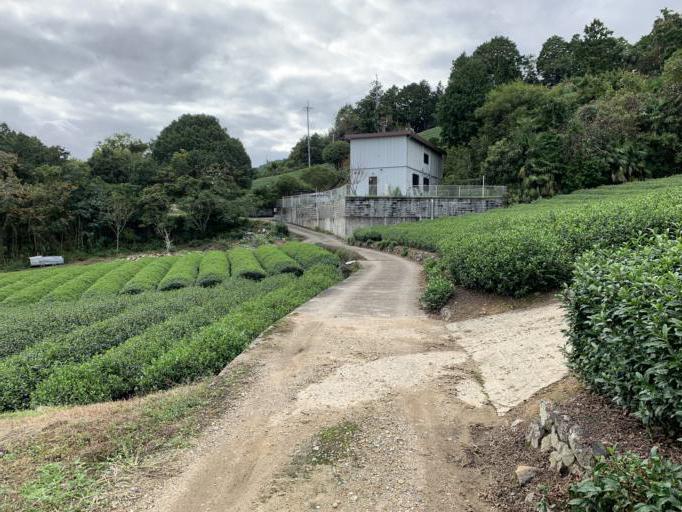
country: JP
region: Kyoto
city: Tanabe
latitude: 34.7844
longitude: 135.8803
